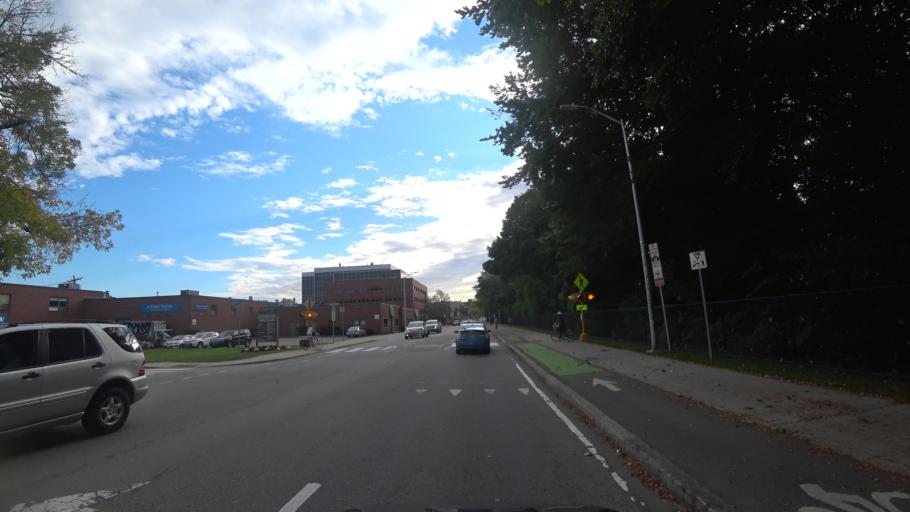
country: US
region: Massachusetts
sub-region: Middlesex County
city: Belmont
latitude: 42.3906
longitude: -71.1544
